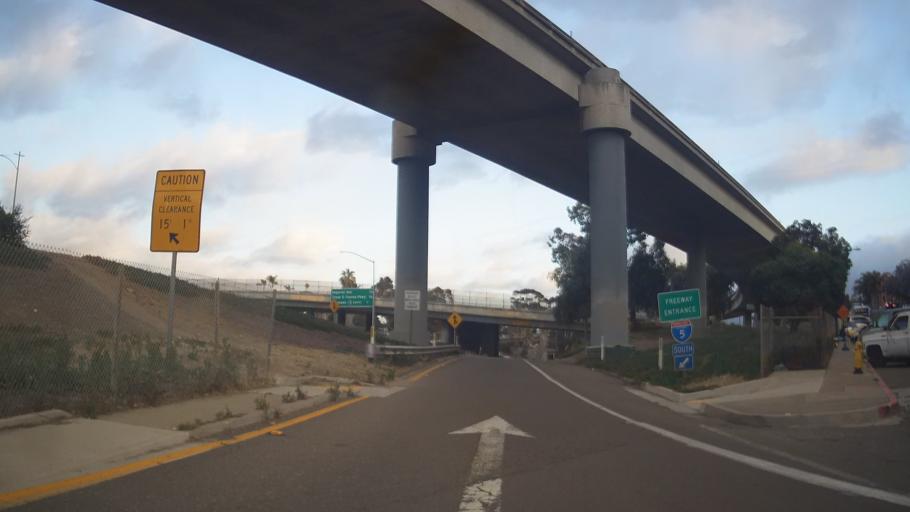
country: US
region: California
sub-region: San Diego County
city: San Diego
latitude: 32.7167
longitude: -117.1485
